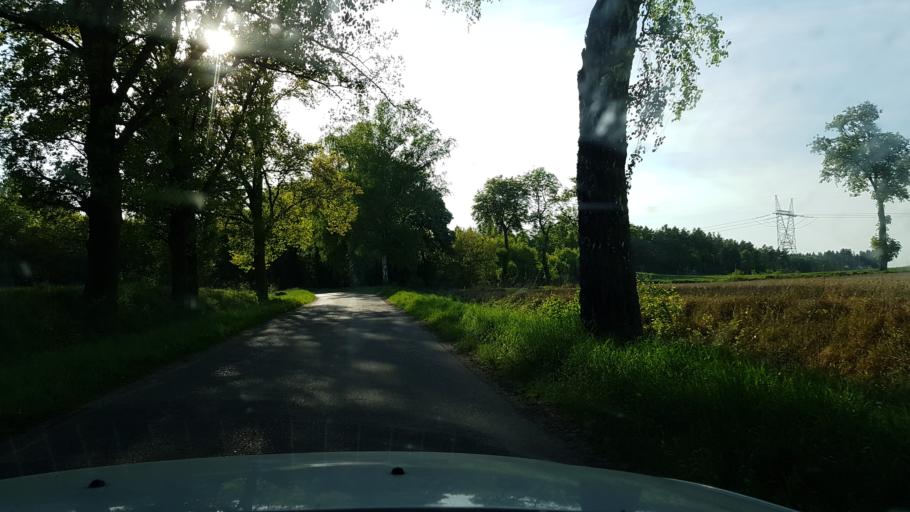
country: PL
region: West Pomeranian Voivodeship
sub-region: Powiat lobeski
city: Dobra
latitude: 53.6357
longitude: 15.3665
